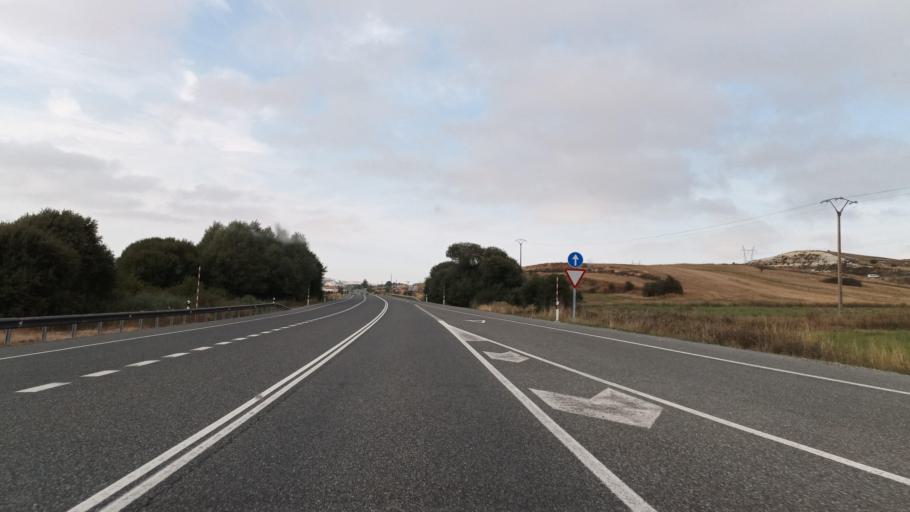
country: ES
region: Castille and Leon
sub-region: Provincia de Burgos
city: Quintanapalla
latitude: 42.4221
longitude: -3.5139
